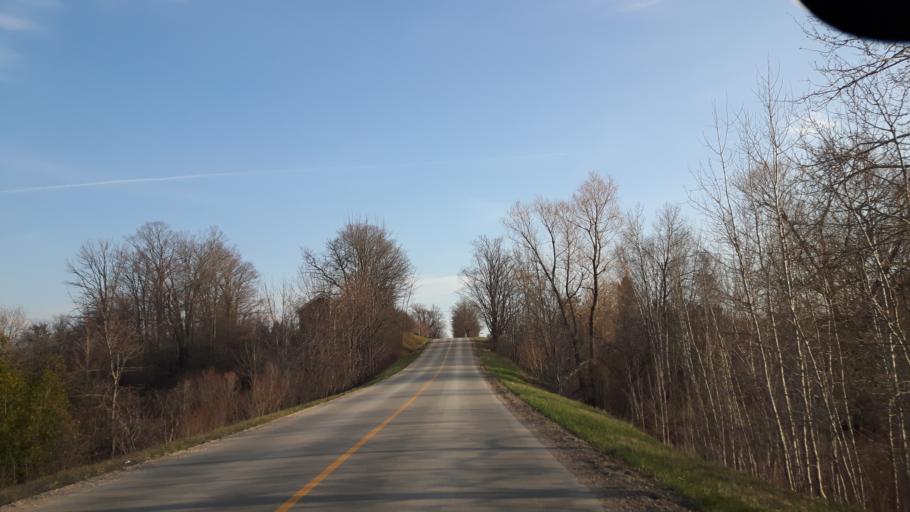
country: CA
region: Ontario
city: Goderich
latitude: 43.6447
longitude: -81.6643
